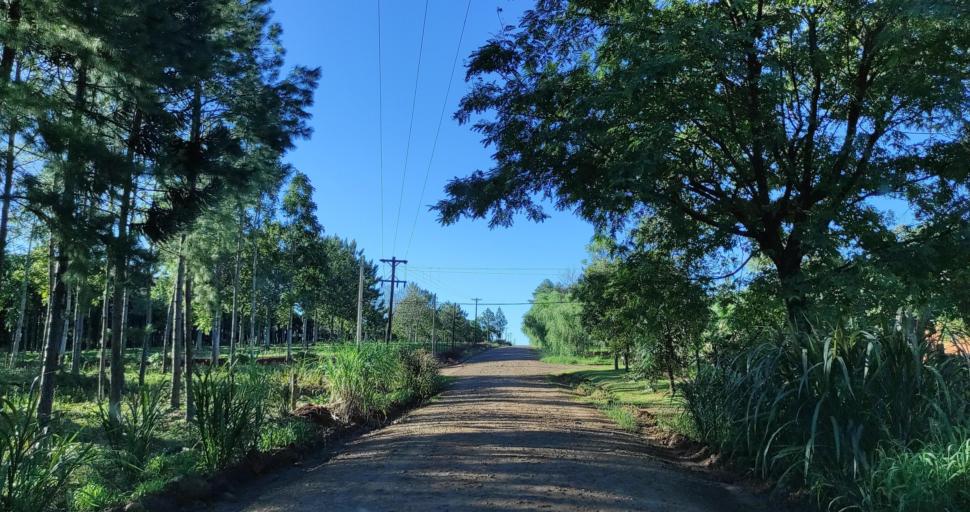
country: AR
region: Misiones
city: Puerto Rico
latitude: -26.8258
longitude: -55.0010
